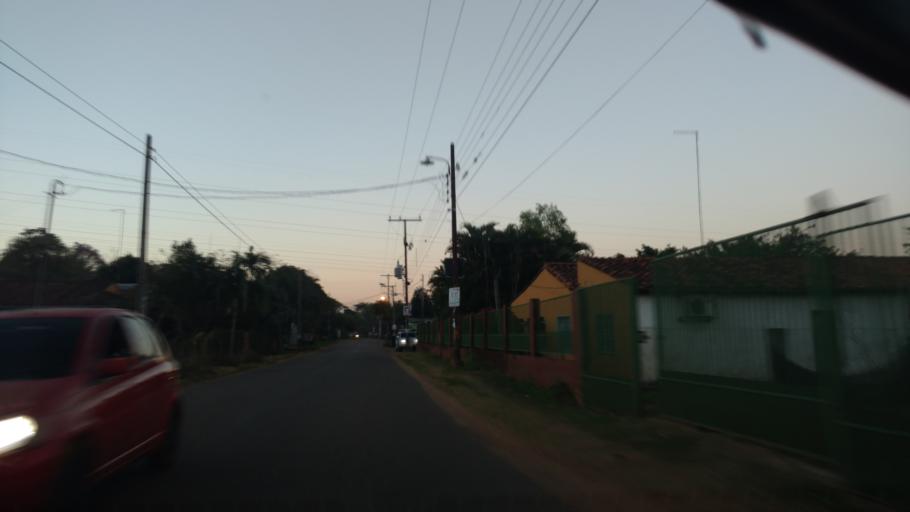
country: PY
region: Central
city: Guarambare
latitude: -25.4706
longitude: -57.4101
